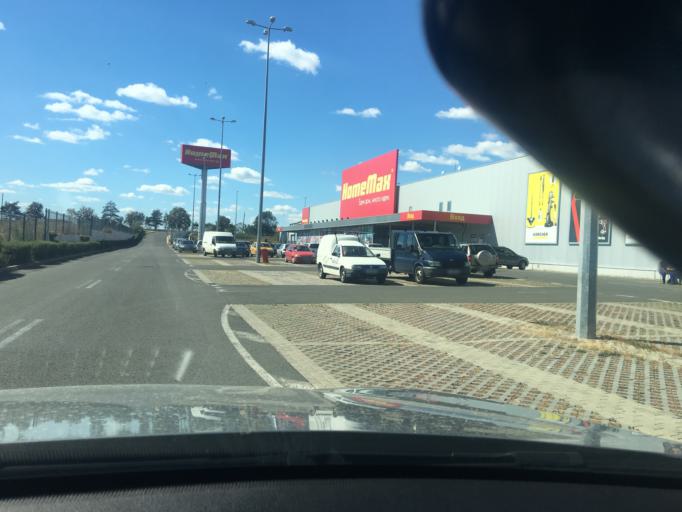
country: BG
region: Burgas
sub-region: Obshtina Burgas
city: Burgas
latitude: 42.5335
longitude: 27.4497
